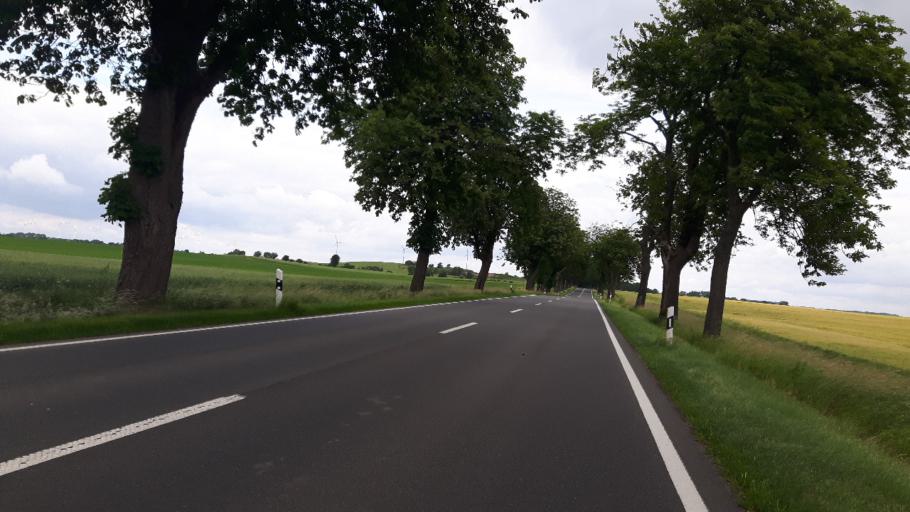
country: DE
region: Brandenburg
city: Mescherin
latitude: 53.2933
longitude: 14.4071
